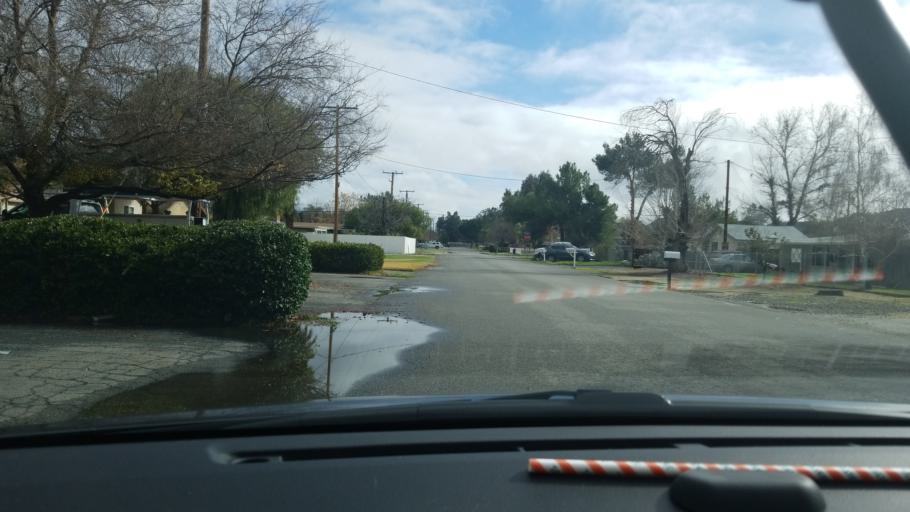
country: US
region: California
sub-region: Riverside County
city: Murrieta
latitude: 33.5522
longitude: -117.2160
